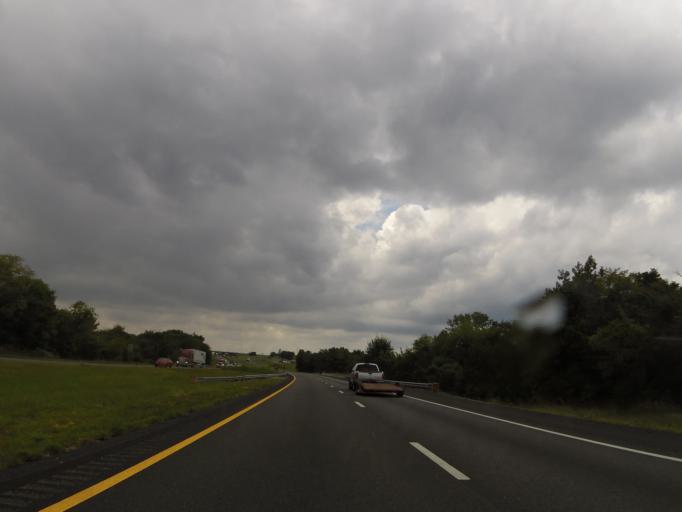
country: US
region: Tennessee
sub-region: Wilson County
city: Watertown
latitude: 36.1886
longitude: -86.1668
